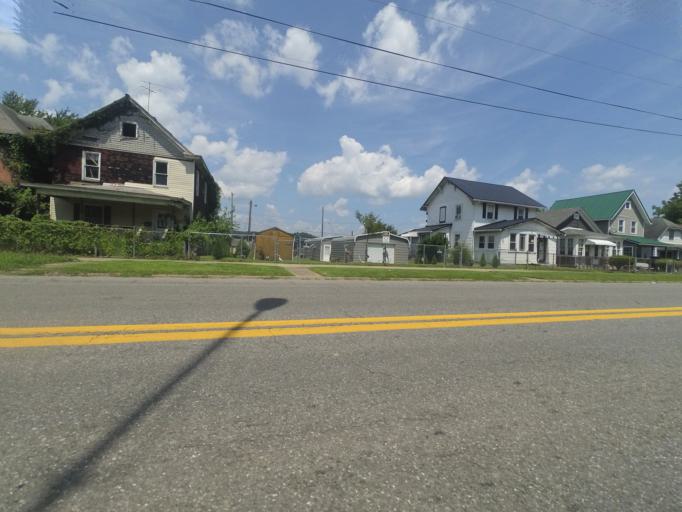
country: US
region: West Virginia
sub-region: Cabell County
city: Huntington
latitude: 38.4194
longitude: -82.4173
